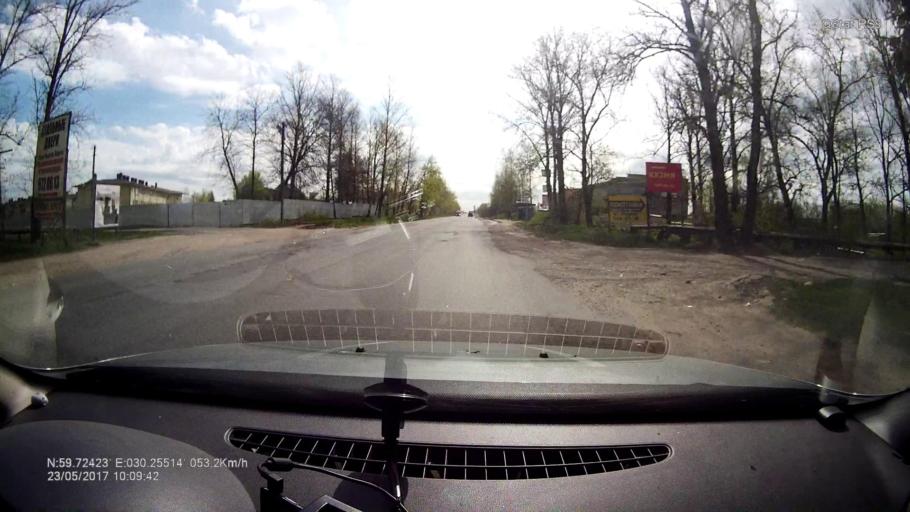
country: RU
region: St.-Petersburg
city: Aleksandrovskaya
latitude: 59.7242
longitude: 30.2554
